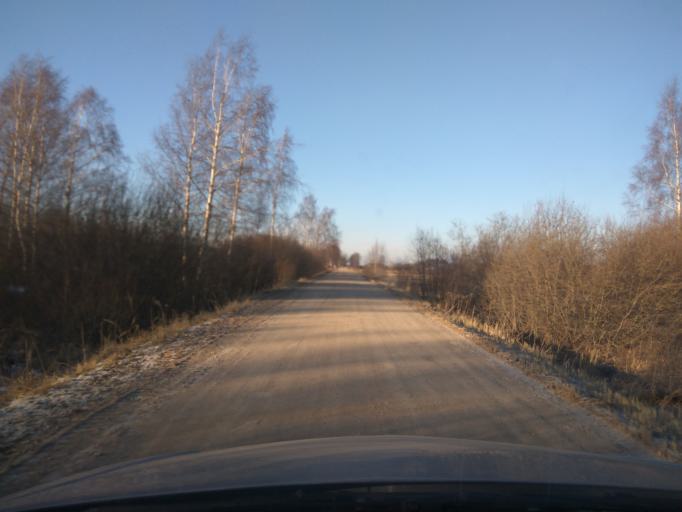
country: LV
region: Kuldigas Rajons
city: Kuldiga
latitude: 56.9686
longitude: 21.9426
